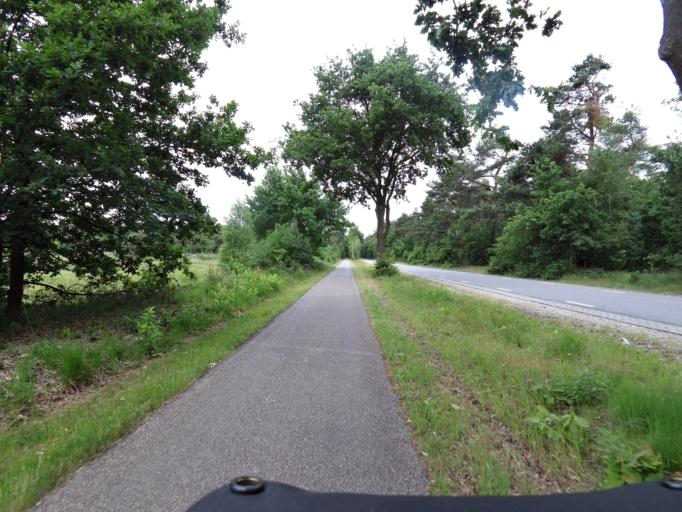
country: NL
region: North Brabant
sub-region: Gemeente Hilvarenbeek
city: Hilvarenbeek
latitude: 51.4104
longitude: 5.1153
